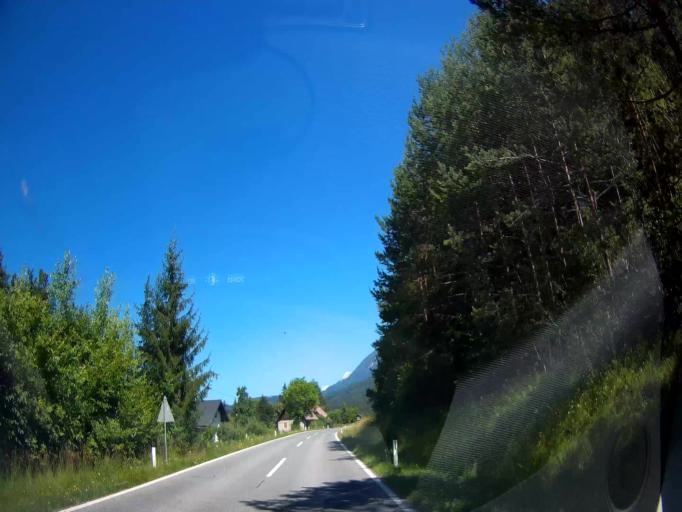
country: AT
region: Carinthia
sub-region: Politischer Bezirk Klagenfurt Land
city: Ebenthal
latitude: 46.5400
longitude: 14.3711
